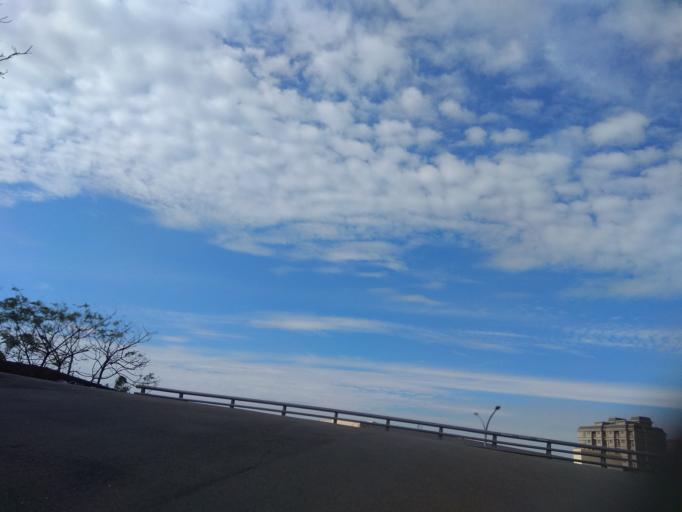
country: TW
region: Taiwan
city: Taoyuan City
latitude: 25.0522
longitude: 121.1788
